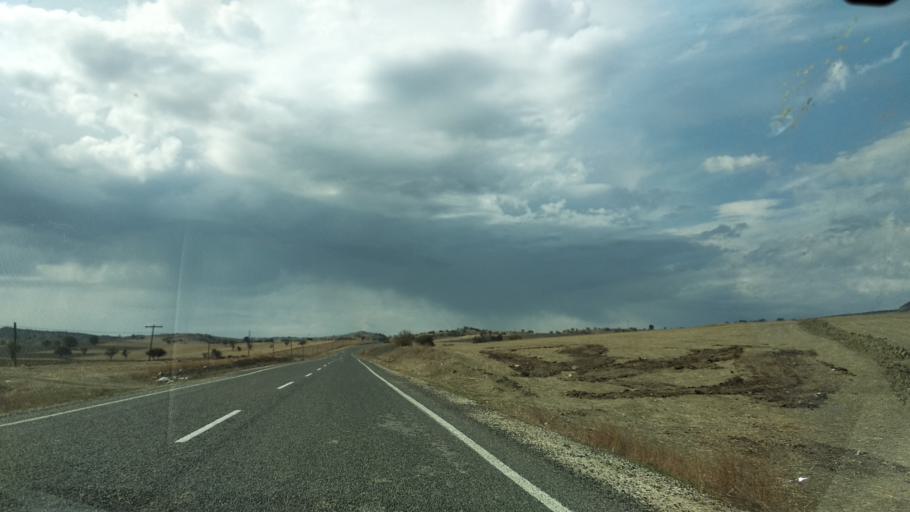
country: TR
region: Bolu
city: Seben
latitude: 40.3917
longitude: 31.5470
